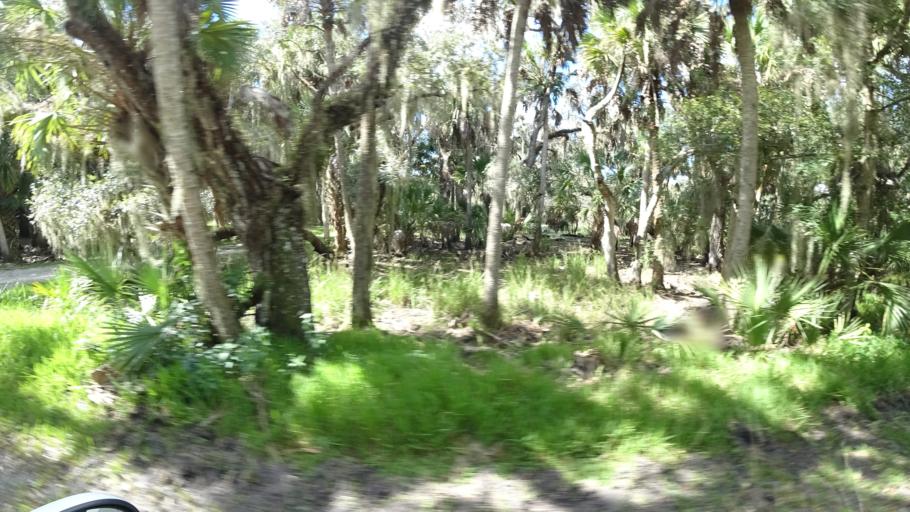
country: US
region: Florida
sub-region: Sarasota County
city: Lake Sarasota
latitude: 27.2619
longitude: -82.2863
